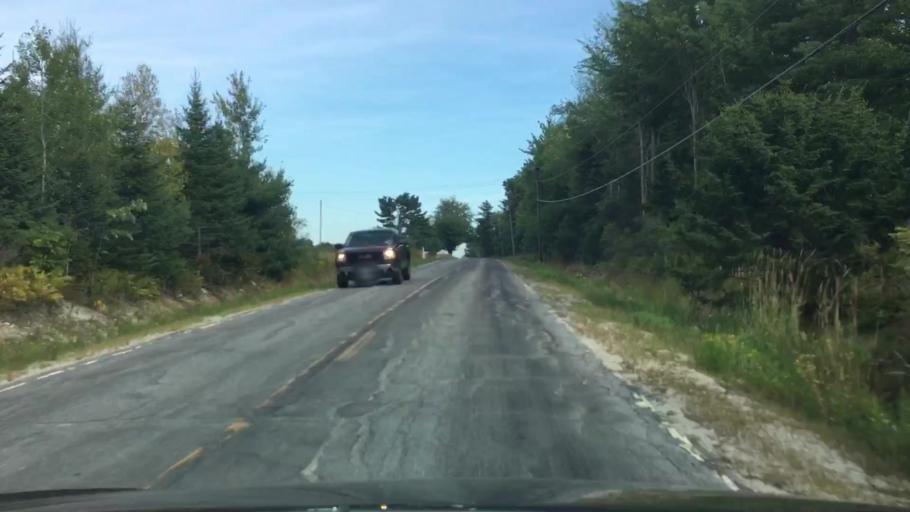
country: US
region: Maine
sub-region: Hancock County
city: Surry
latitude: 44.5053
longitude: -68.5898
